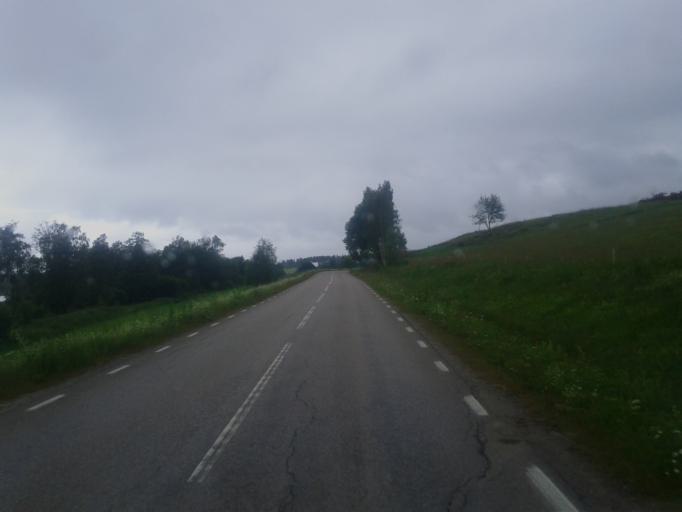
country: SE
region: Gaevleborg
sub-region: Nordanstigs Kommun
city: Bergsjoe
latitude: 61.9792
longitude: 17.2812
